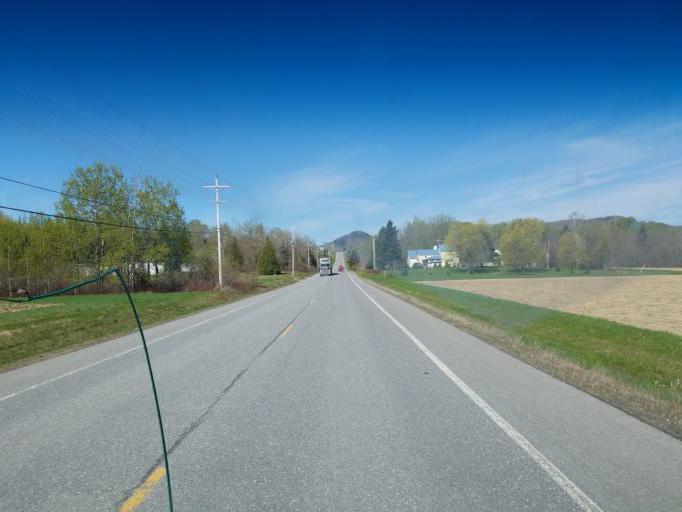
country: US
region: Maine
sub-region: Aroostook County
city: Presque Isle
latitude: 46.6669
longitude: -68.2011
